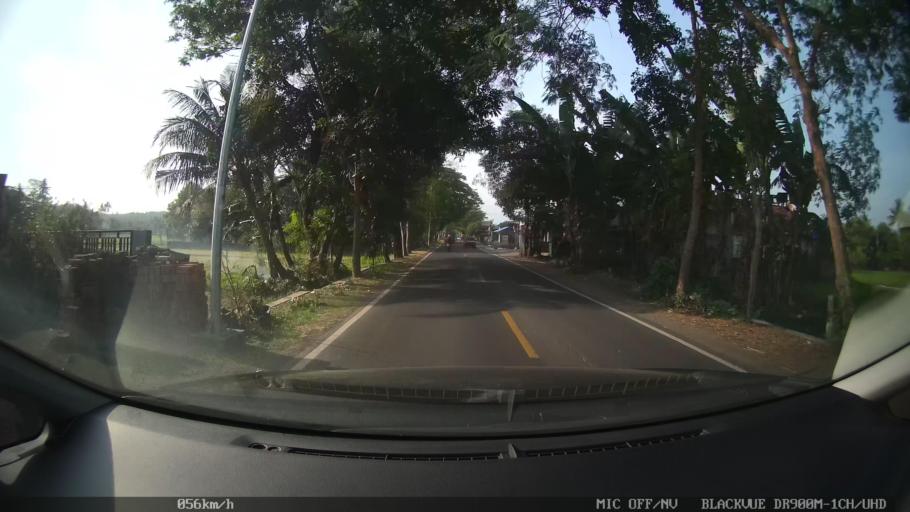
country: ID
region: Daerah Istimewa Yogyakarta
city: Bantul
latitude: -7.8814
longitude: 110.3194
